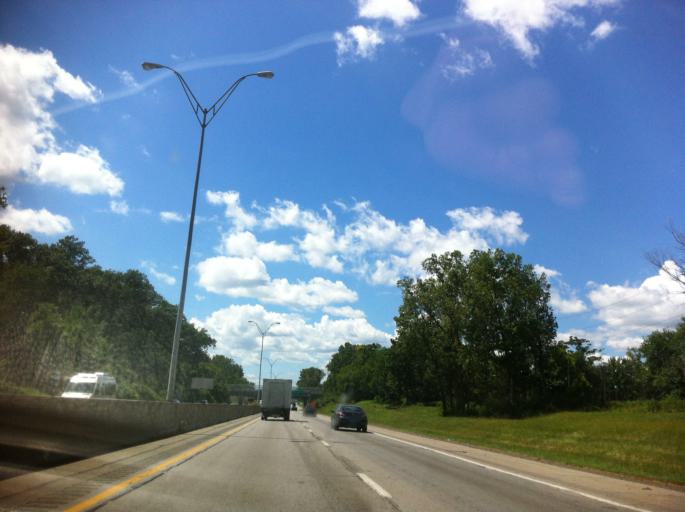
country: US
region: Ohio
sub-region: Lucas County
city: Ottawa Hills
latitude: 41.6884
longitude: -83.6319
